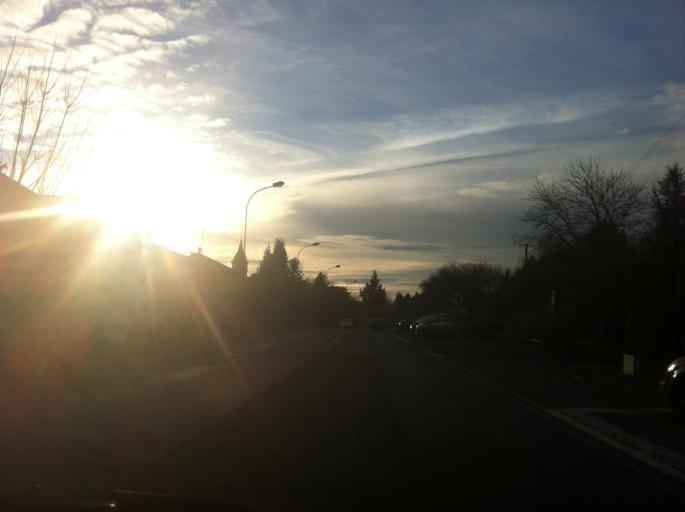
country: FR
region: Aquitaine
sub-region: Departement de la Dordogne
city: Mensignac
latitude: 45.2277
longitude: 0.5569
